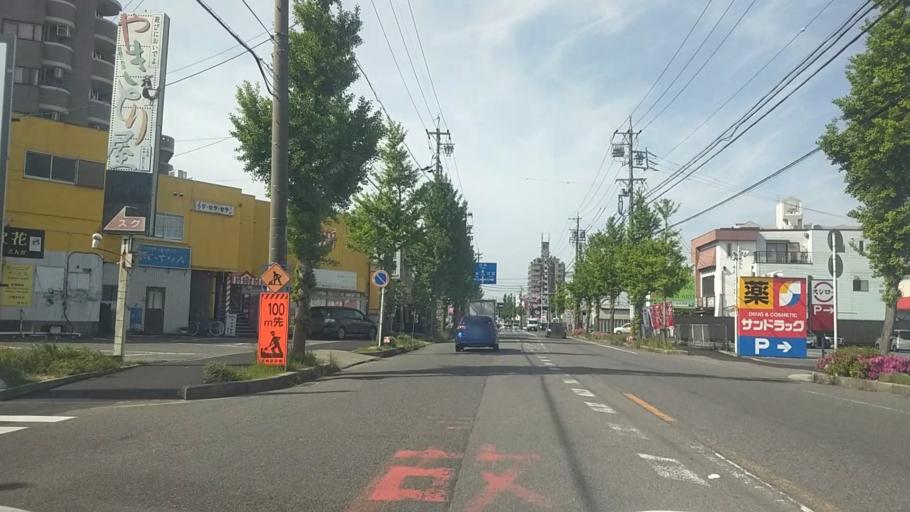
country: JP
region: Aichi
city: Okazaki
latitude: 34.9356
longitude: 137.1466
